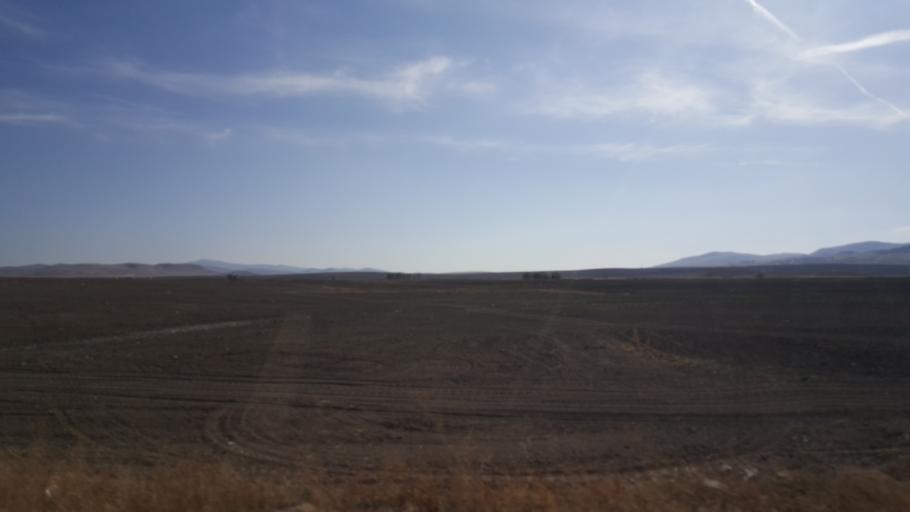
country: TR
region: Ankara
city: Yenice
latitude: 39.3793
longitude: 32.7571
